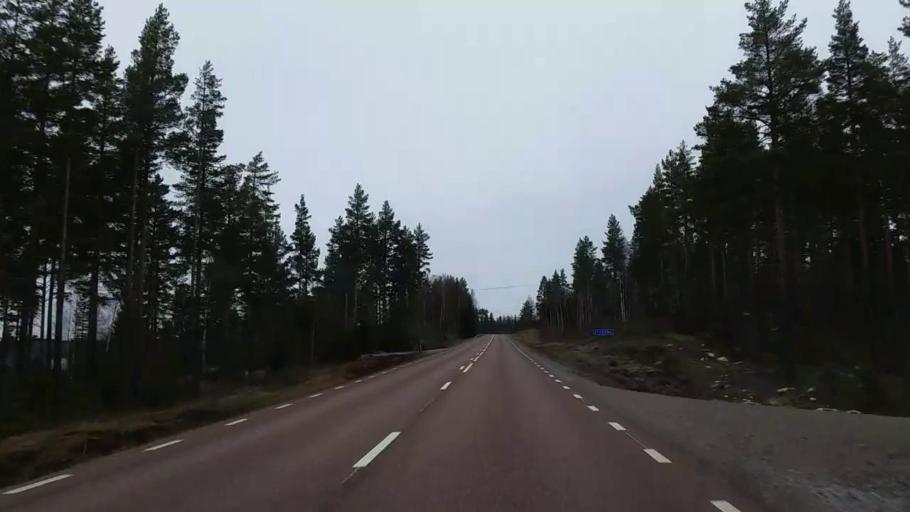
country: SE
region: Gaevleborg
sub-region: Ovanakers Kommun
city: Edsbyn
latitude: 61.2218
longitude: 15.8767
